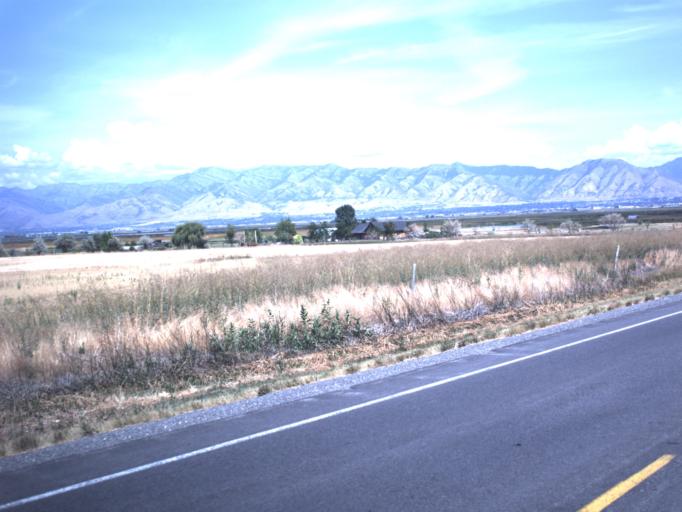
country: US
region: Utah
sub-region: Cache County
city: Mendon
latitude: 41.7478
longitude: -111.9671
